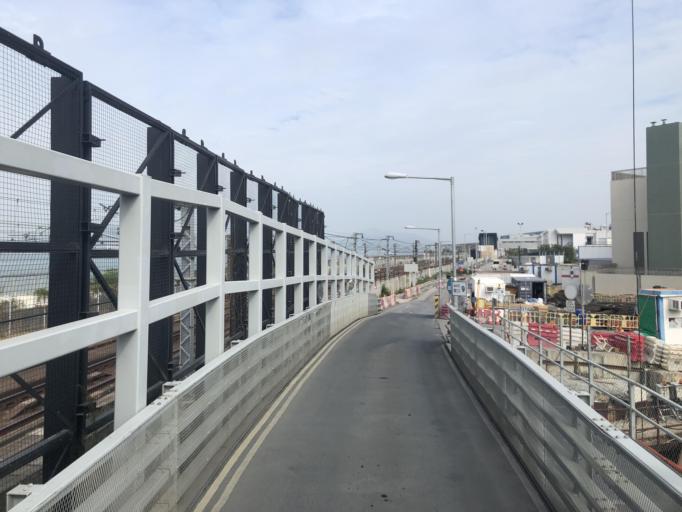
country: HK
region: Tuen Mun
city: Tuen Mun
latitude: 22.3208
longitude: 113.9373
